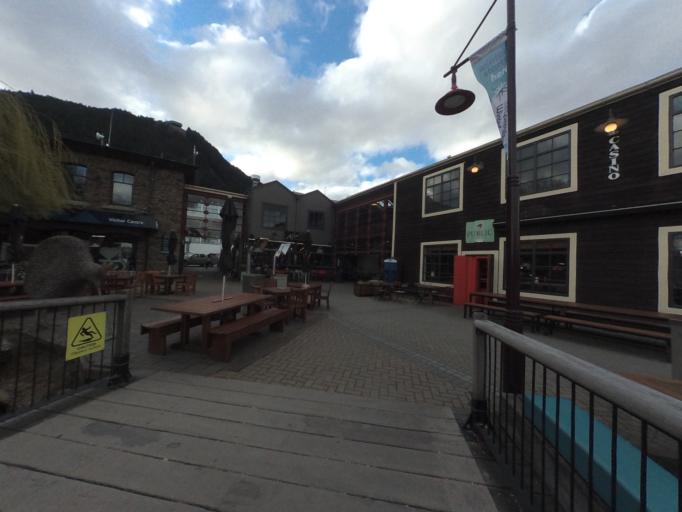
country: NZ
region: Otago
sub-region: Queenstown-Lakes District
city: Queenstown
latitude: -45.0334
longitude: 168.6580
